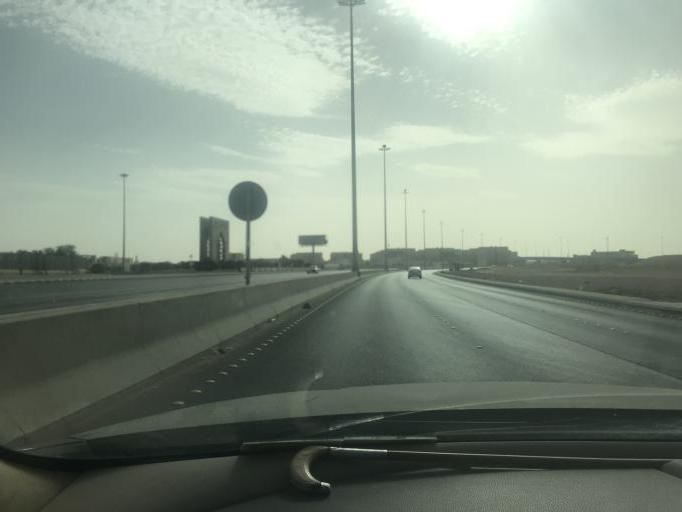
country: SA
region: Ar Riyad
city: Riyadh
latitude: 24.8201
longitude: 46.7069
